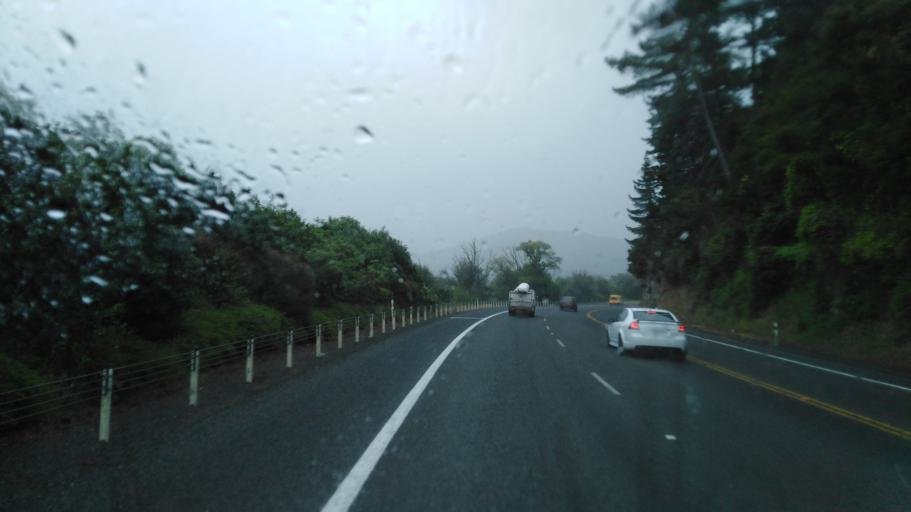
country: NZ
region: Marlborough
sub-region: Marlborough District
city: Picton
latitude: -41.3798
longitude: 173.9472
